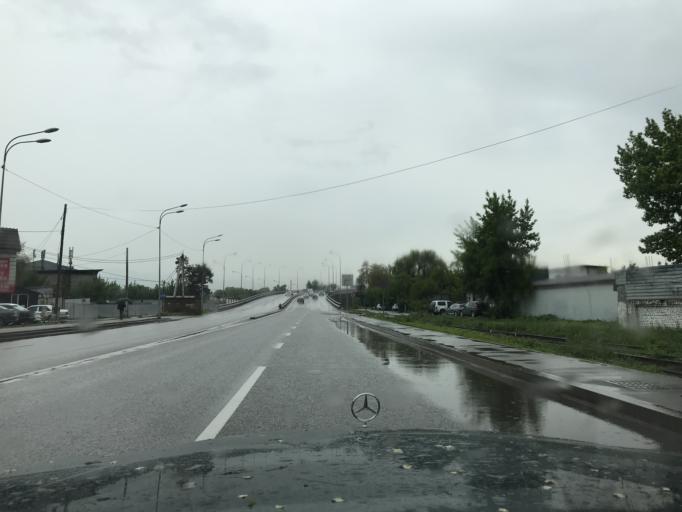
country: KZ
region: Almaty Oblysy
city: Pervomayskiy
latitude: 43.3407
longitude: 76.9662
